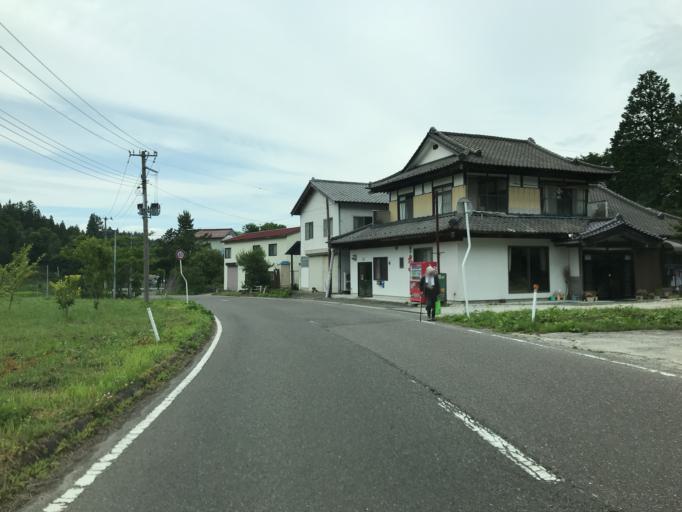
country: JP
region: Fukushima
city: Funehikimachi-funehiki
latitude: 37.3992
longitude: 140.6941
